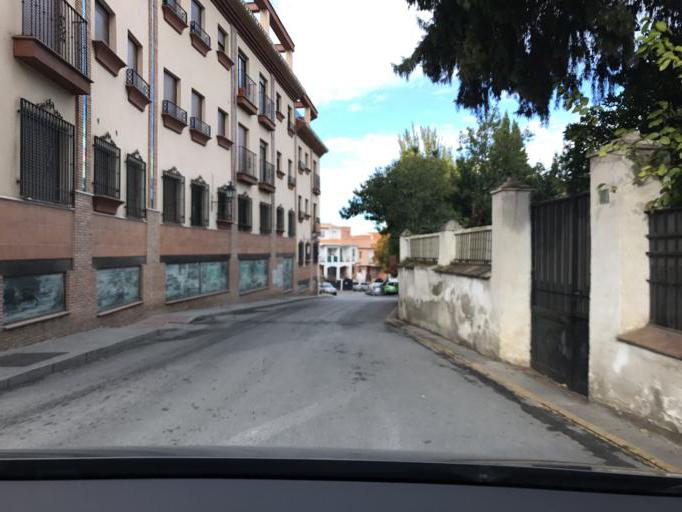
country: ES
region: Andalusia
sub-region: Provincia de Granada
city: Zubia
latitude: 37.1216
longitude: -3.5853
